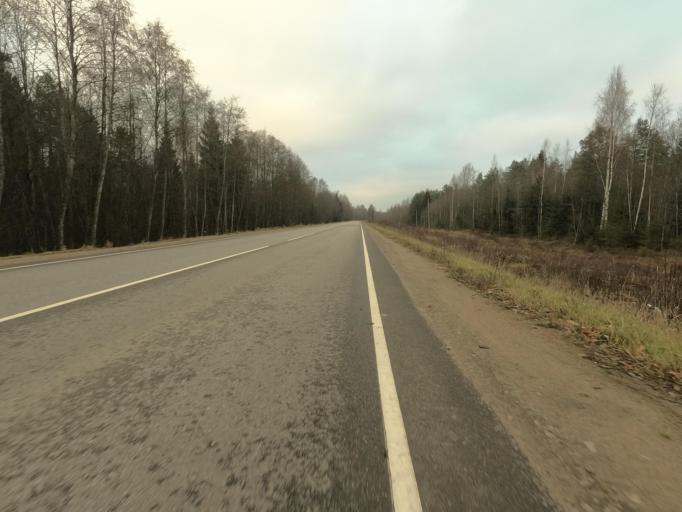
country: RU
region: Leningrad
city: Pavlovo
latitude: 59.8054
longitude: 30.9563
